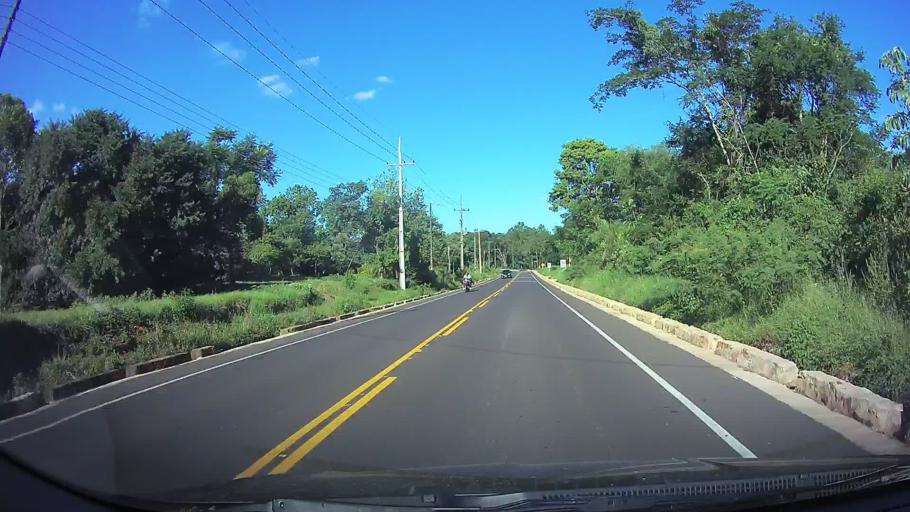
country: PY
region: Cordillera
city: Caacupe
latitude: -25.3223
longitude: -57.1509
